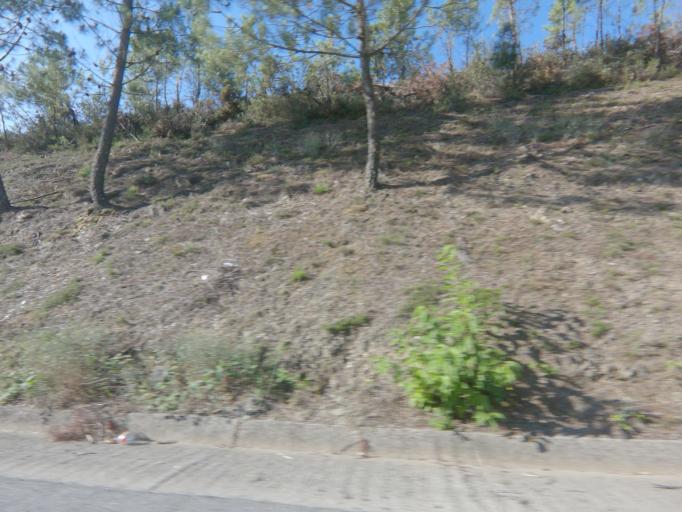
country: PT
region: Vila Real
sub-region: Sabrosa
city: Sabrosa
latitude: 41.2622
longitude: -7.6099
